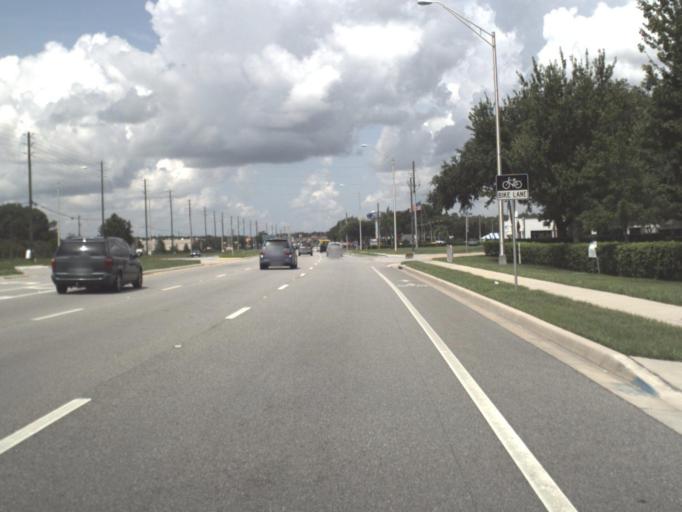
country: US
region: Florida
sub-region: Pasco County
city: Wesley Chapel
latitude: 28.2398
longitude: -82.3377
